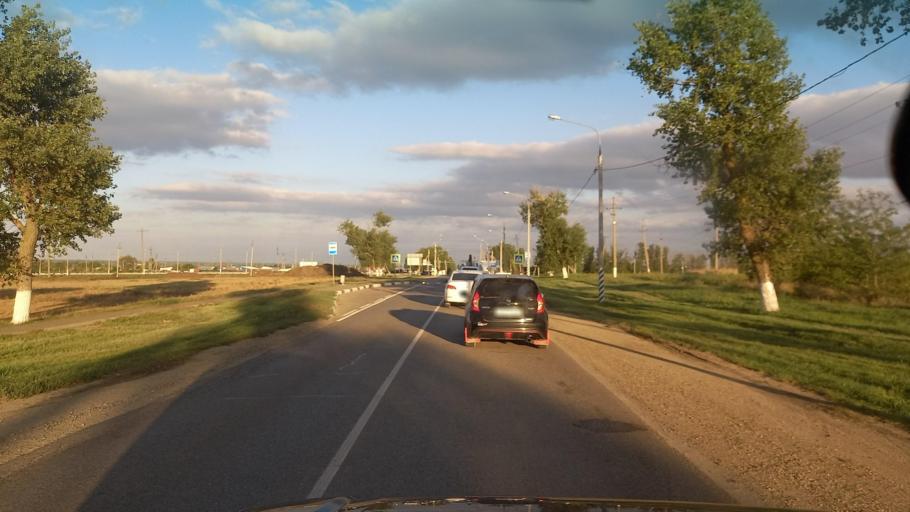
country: RU
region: Krasnodarskiy
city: Krymsk
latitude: 44.9379
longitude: 37.9589
